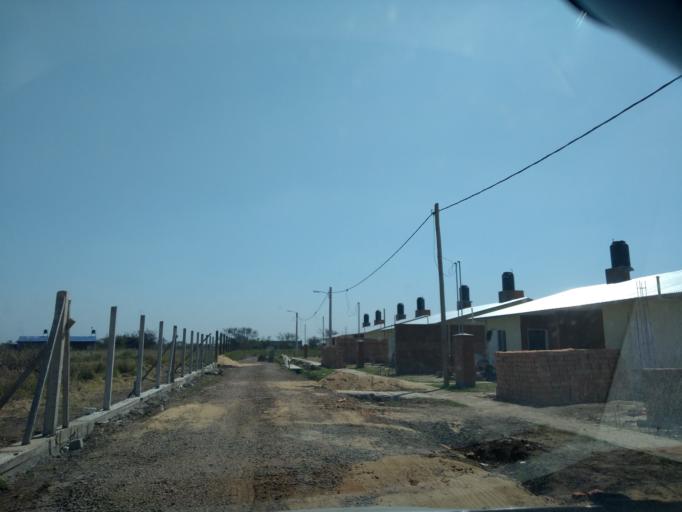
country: AR
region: Chaco
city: Fontana
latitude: -27.4077
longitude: -58.9750
